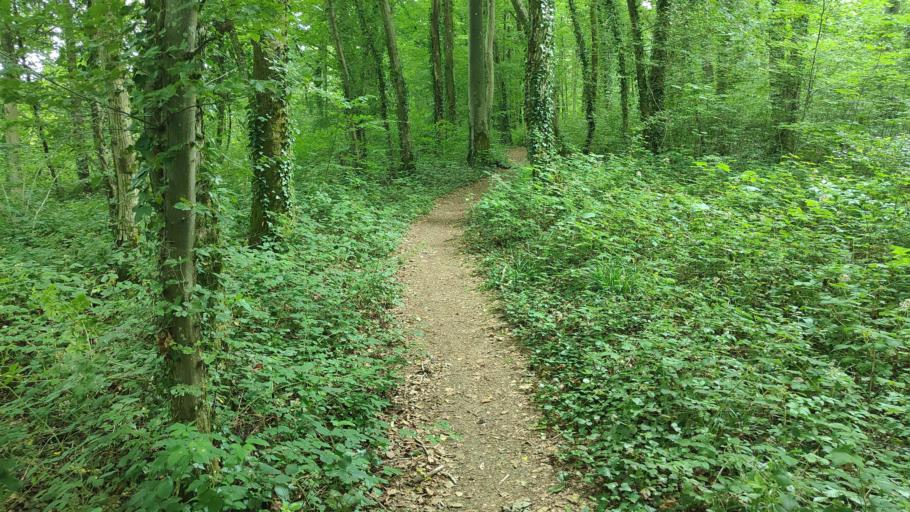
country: BE
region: Wallonia
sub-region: Province du Hainaut
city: Chimay
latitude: 50.0589
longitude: 4.3922
